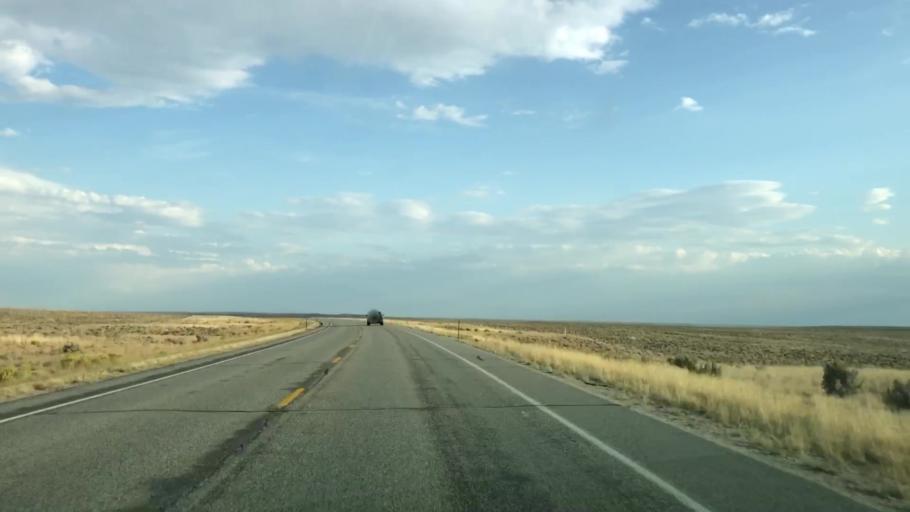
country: US
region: Wyoming
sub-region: Sublette County
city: Marbleton
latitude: 42.3386
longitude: -109.5211
